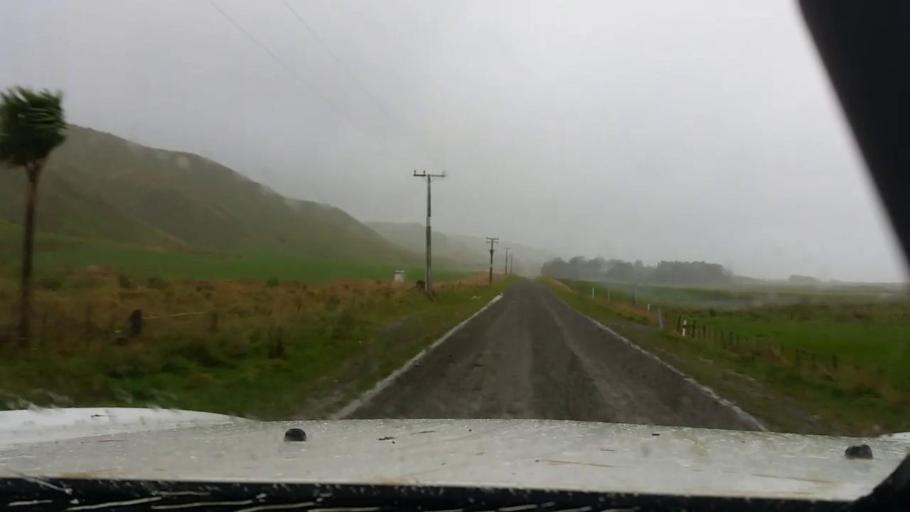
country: NZ
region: Wellington
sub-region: Masterton District
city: Masterton
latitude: -41.2567
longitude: 175.9050
